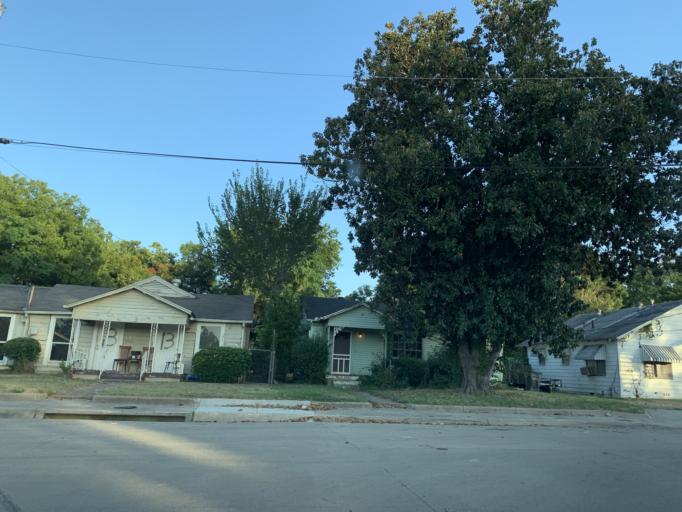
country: US
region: Texas
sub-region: Dallas County
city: Dallas
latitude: 32.7662
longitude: -96.7467
